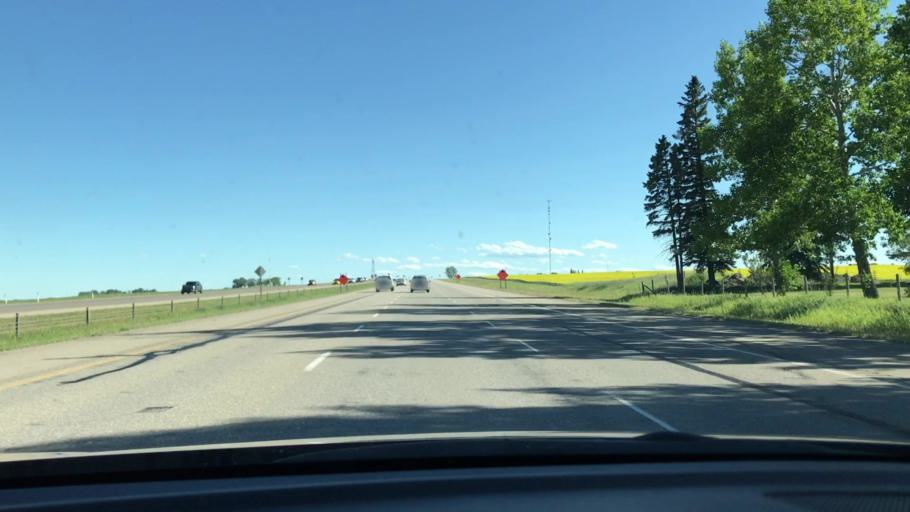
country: CA
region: Alberta
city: Crossfield
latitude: 51.4305
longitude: -114.0020
